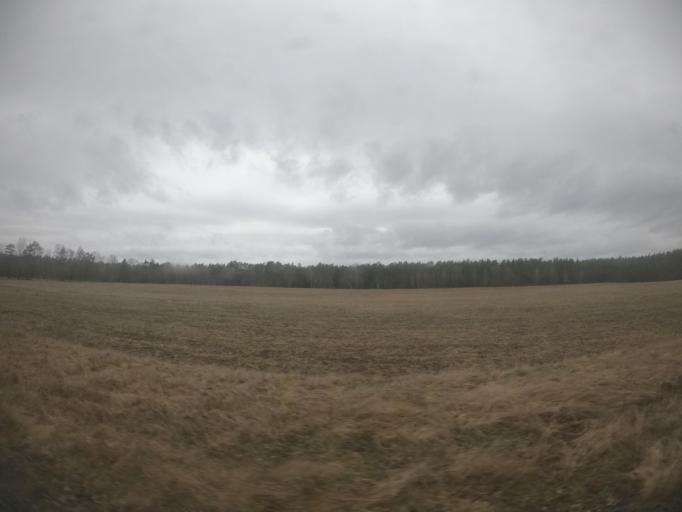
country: PL
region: West Pomeranian Voivodeship
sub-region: Powiat szczecinecki
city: Bialy Bor
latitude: 53.8260
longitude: 16.8719
